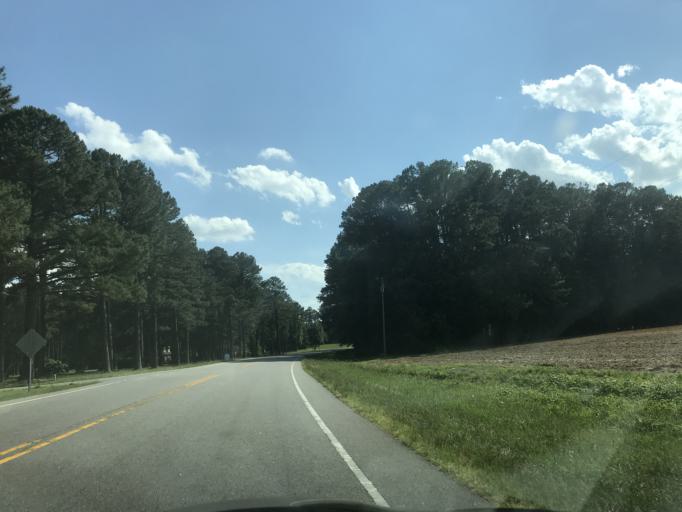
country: US
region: North Carolina
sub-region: Nash County
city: Spring Hope
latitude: 35.9380
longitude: -78.1193
